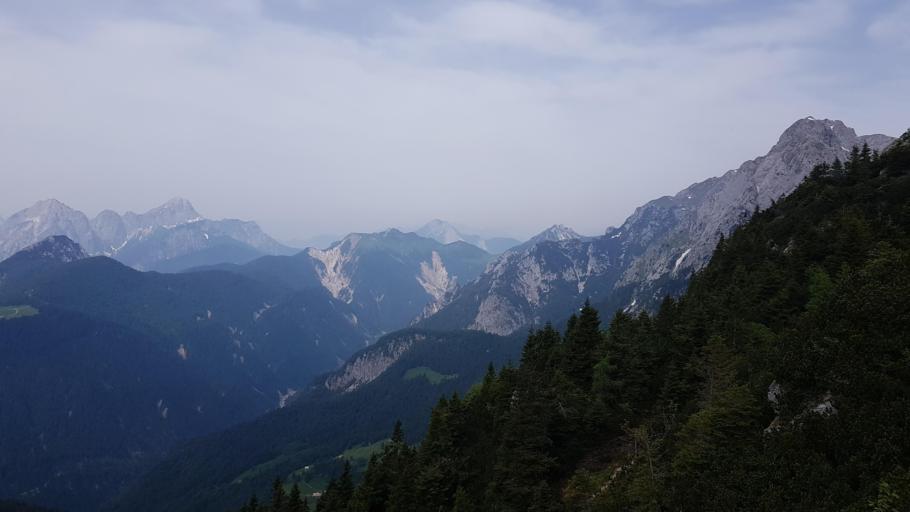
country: IT
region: Friuli Venezia Giulia
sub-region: Provincia di Udine
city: Pontebba
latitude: 46.5405
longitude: 13.2846
